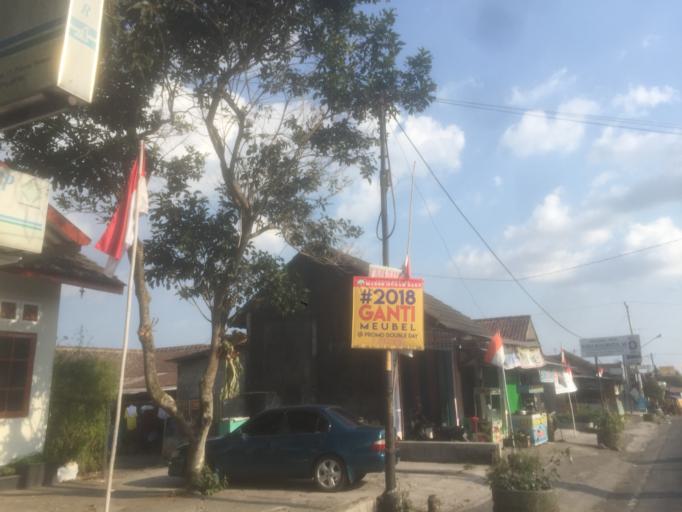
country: ID
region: Daerah Istimewa Yogyakarta
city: Sleman
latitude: -7.6641
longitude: 110.4200
